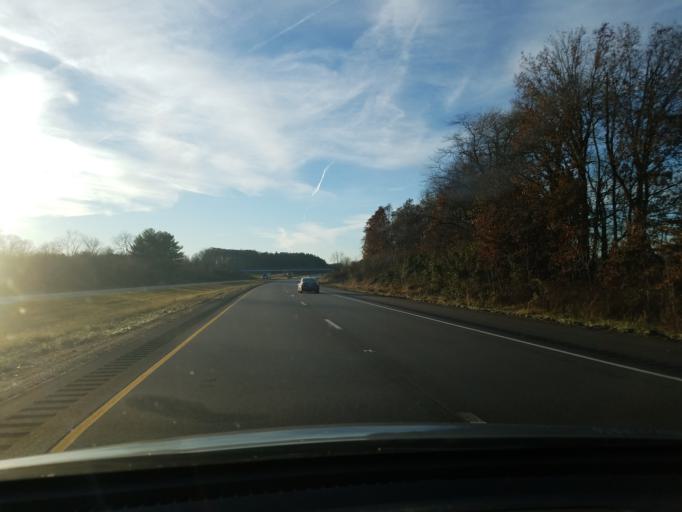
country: US
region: Indiana
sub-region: Spencer County
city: Dale
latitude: 38.1988
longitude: -87.0855
